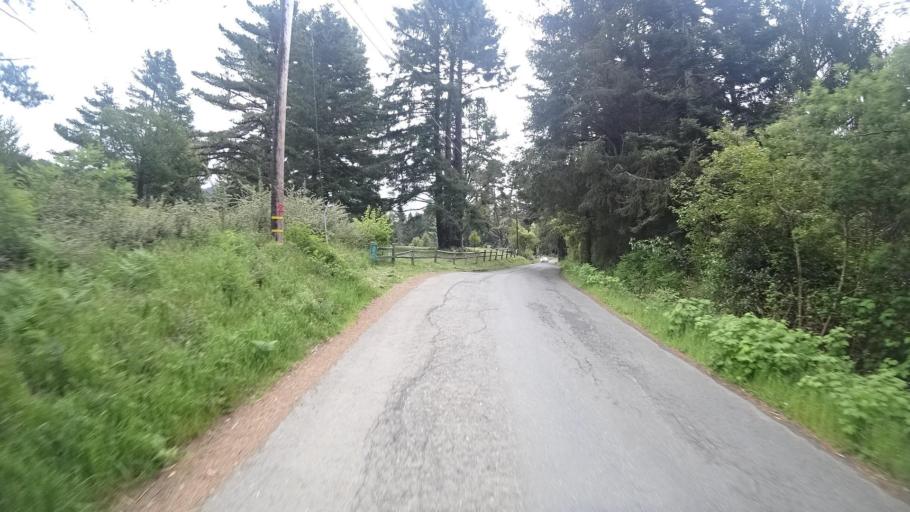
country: US
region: California
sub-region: Humboldt County
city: Bayside
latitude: 40.8485
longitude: -124.0546
